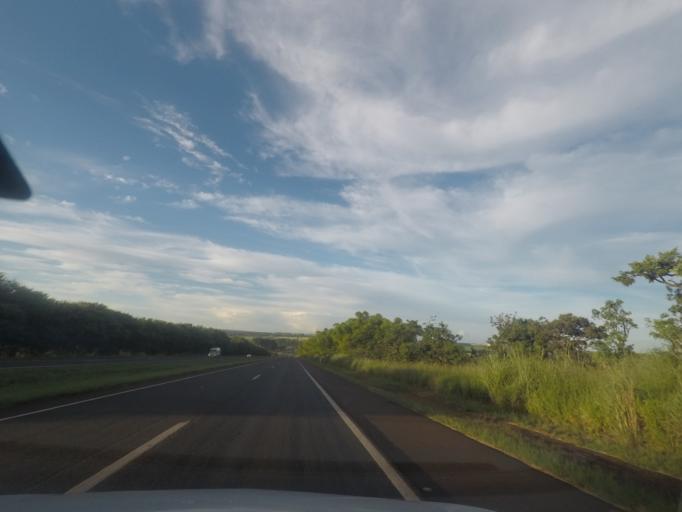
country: BR
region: Goias
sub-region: Goiatuba
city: Goiatuba
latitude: -18.0246
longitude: -49.2642
